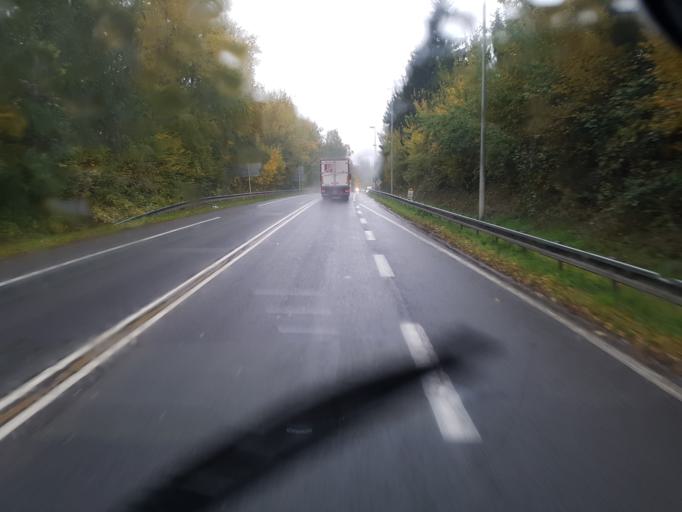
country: FR
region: Picardie
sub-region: Departement de l'Aisne
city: Harly
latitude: 49.8268
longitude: 3.2986
